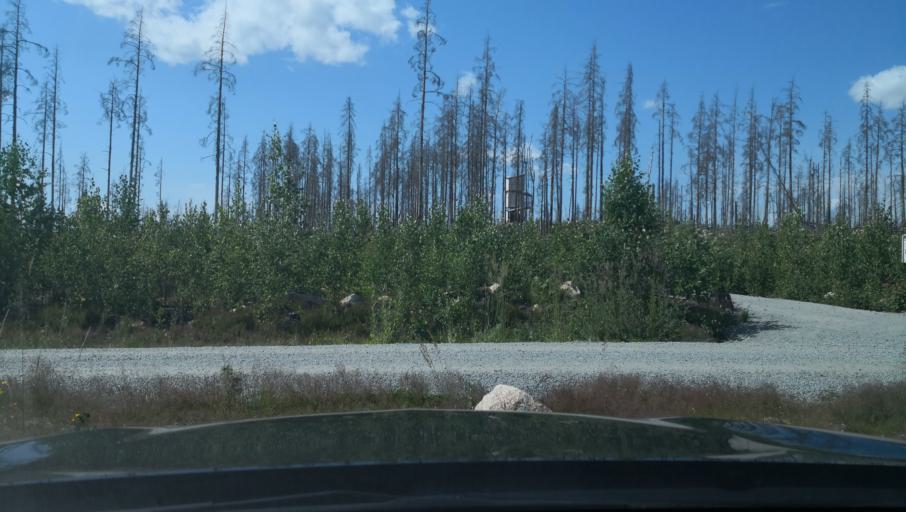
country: SE
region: Vaestmanland
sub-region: Surahammars Kommun
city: Ramnas
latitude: 59.9127
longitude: 16.1499
